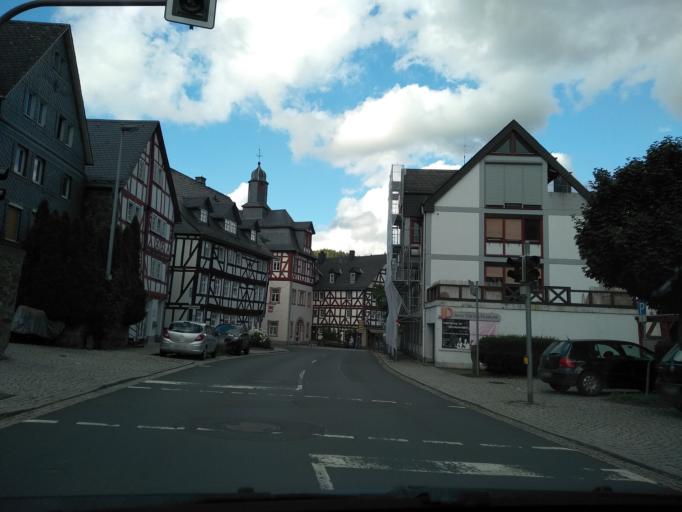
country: DE
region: Hesse
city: Dillenburg
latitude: 50.7390
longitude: 8.2841
